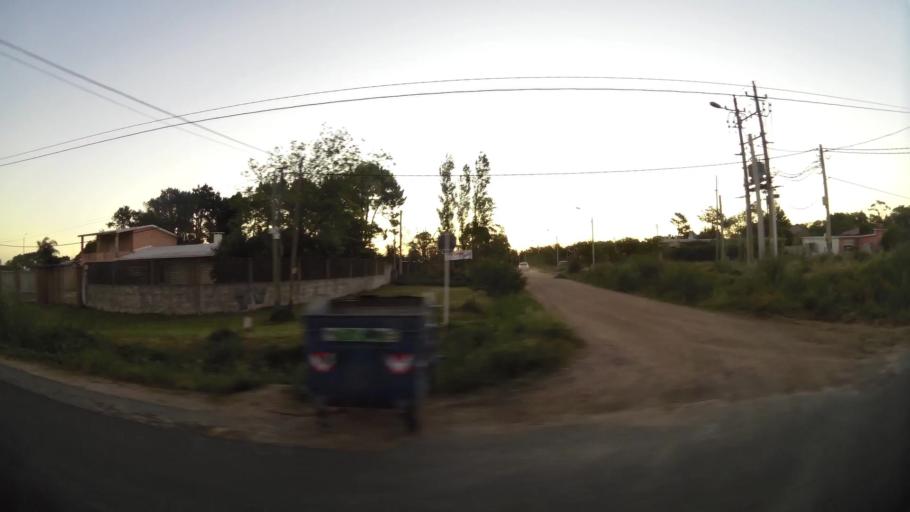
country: UY
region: Canelones
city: Barra de Carrasco
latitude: -34.8273
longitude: -55.9425
